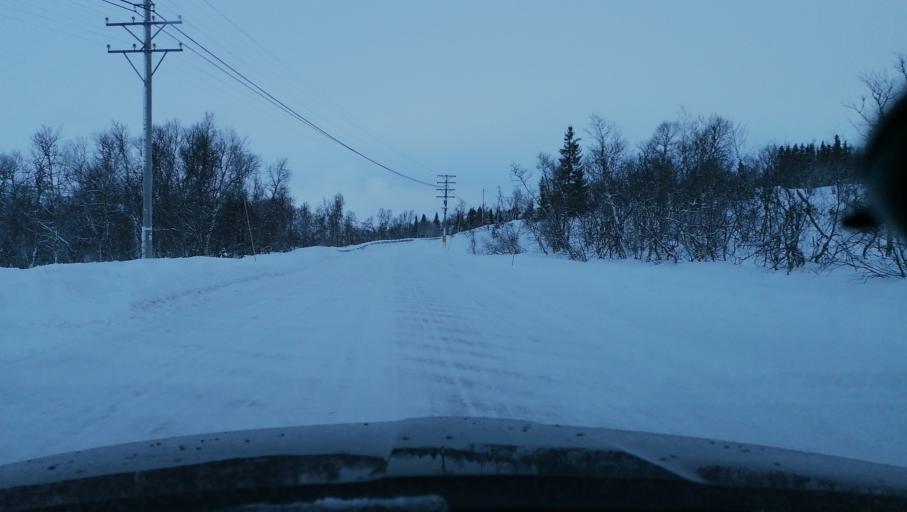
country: NO
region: Aust-Agder
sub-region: Bykle
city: Hovden
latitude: 59.6379
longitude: 7.4537
